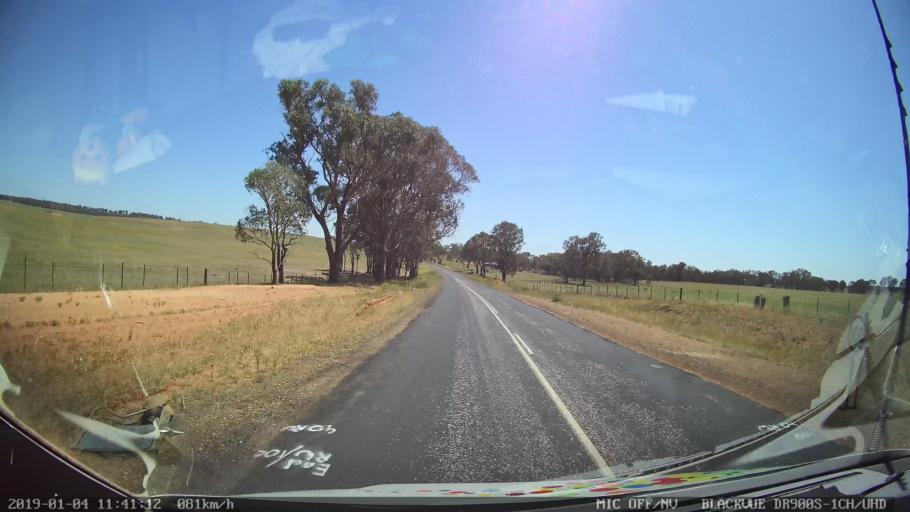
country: AU
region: New South Wales
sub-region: Cabonne
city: Molong
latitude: -32.9965
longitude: 148.7870
